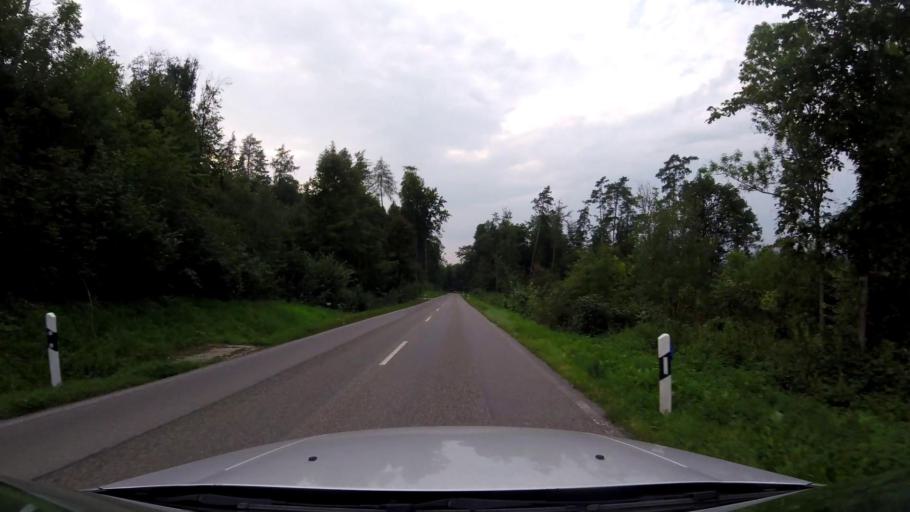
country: DE
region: Baden-Wuerttemberg
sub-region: Regierungsbezirk Stuttgart
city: Allmersbach im Tal
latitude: 48.8969
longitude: 9.4936
